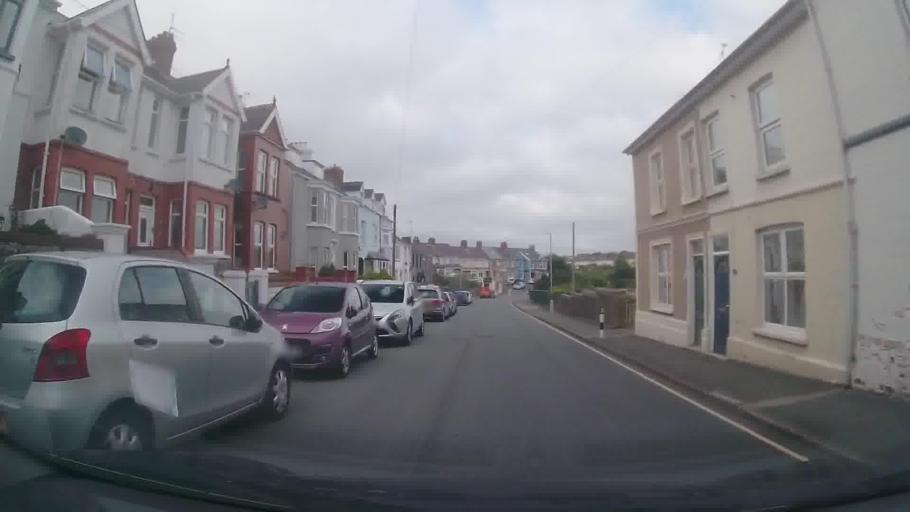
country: GB
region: Wales
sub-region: Pembrokeshire
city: Milford Haven
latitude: 51.7126
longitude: -5.0447
